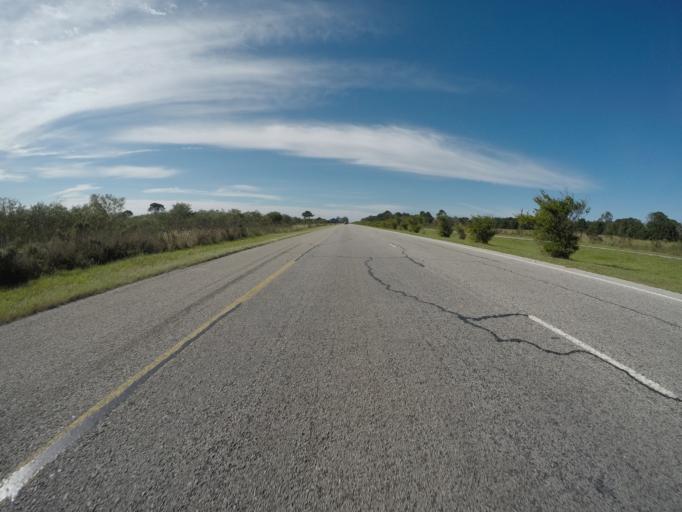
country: ZA
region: Eastern Cape
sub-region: Nelson Mandela Bay Metropolitan Municipality
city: Uitenhage
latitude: -33.9333
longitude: 25.3555
